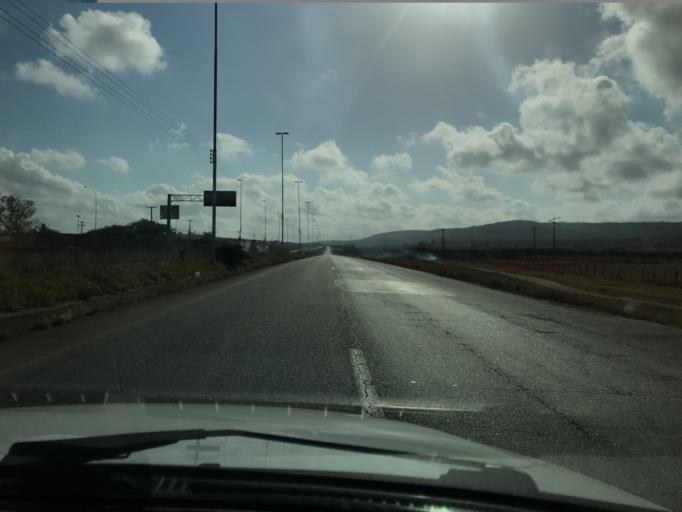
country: BR
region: Pernambuco
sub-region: Bezerros
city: Bezerros
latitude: -8.2365
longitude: -35.7315
